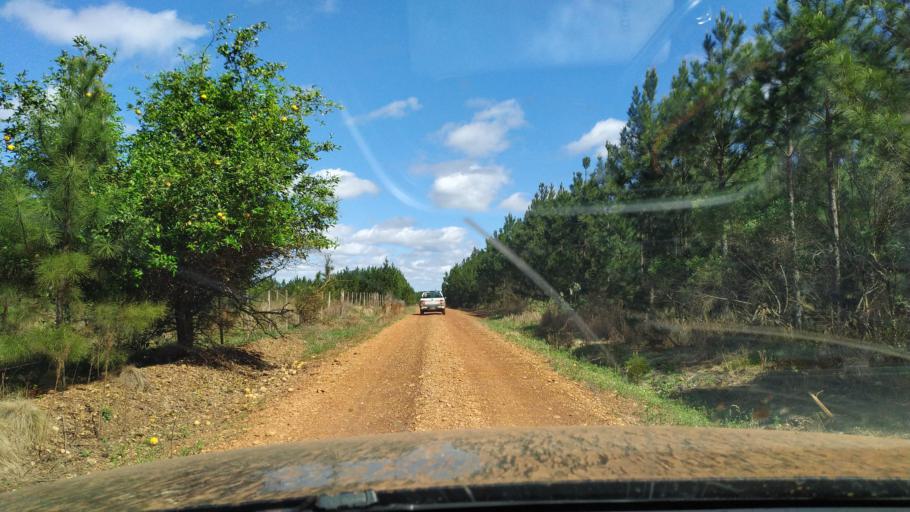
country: AR
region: Corrientes
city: Santo Tome
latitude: -28.4633
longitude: -55.9745
